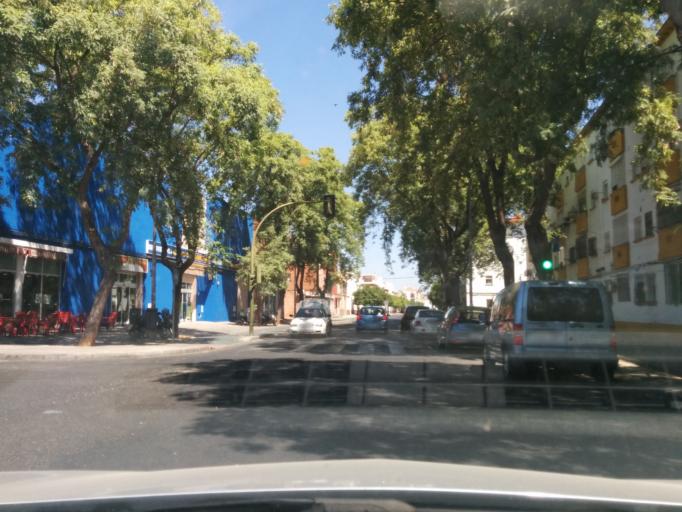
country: ES
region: Andalusia
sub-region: Provincia de Sevilla
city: Sevilla
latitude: 37.3662
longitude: -5.9752
